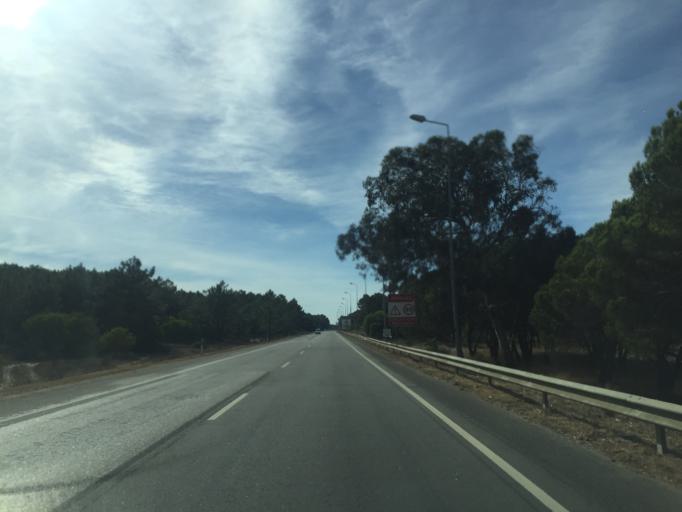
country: PT
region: Coimbra
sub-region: Figueira da Foz
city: Lavos
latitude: 40.0975
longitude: -8.8547
